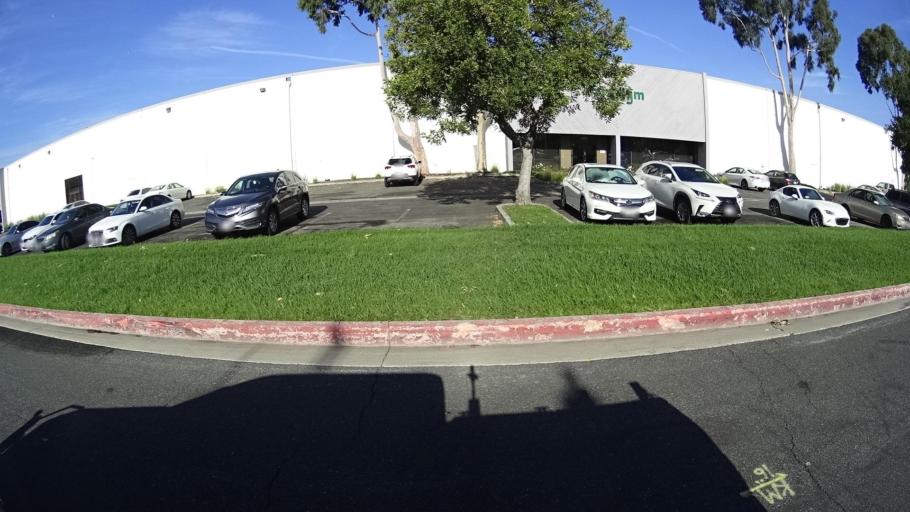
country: US
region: California
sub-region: Los Angeles County
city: South San Jose Hills
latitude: 33.9955
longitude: -117.9010
